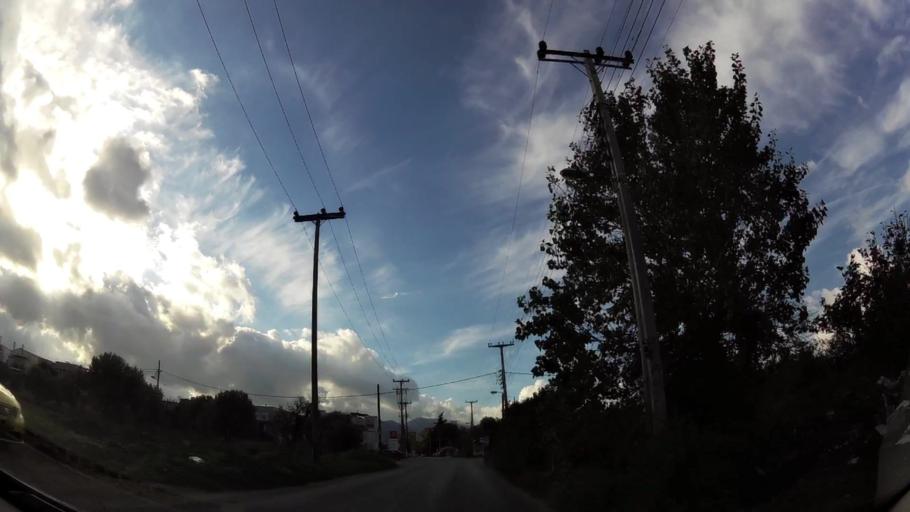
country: GR
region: Attica
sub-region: Nomarchia Athinas
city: Vrilissia
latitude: 38.0417
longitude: 23.8194
